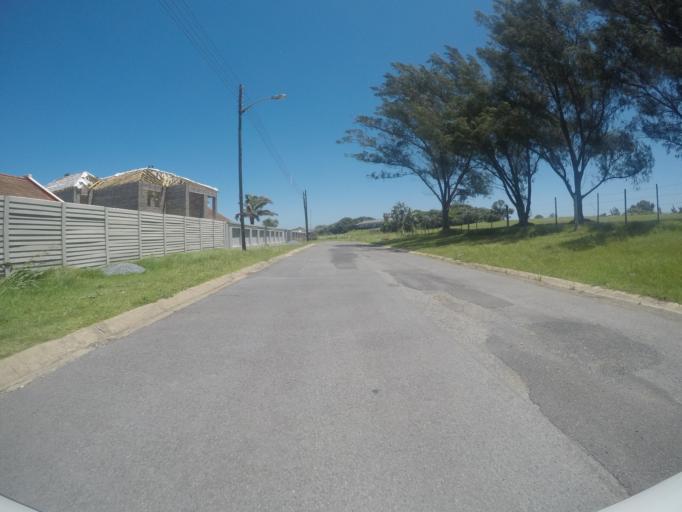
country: ZA
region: Eastern Cape
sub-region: Buffalo City Metropolitan Municipality
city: East London
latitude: -32.9514
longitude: 28.0089
